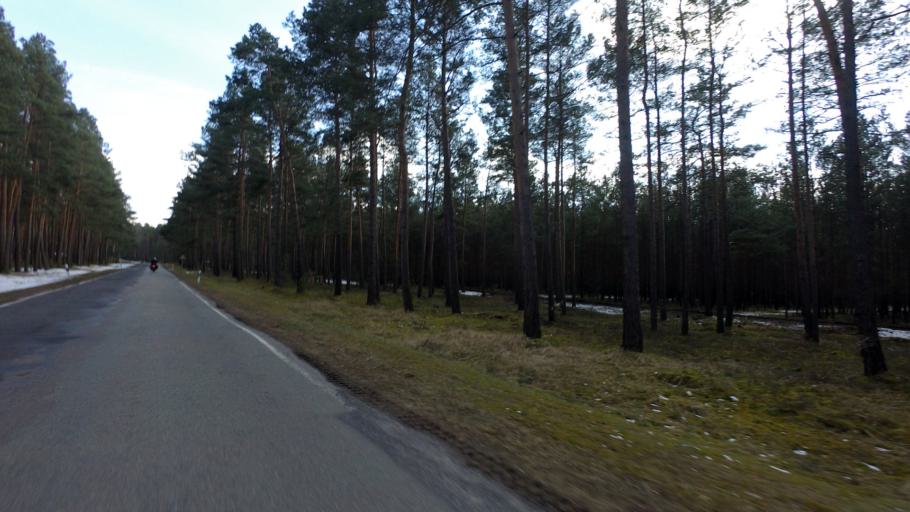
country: DE
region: Brandenburg
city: Marienwerder
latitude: 52.8019
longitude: 13.5907
